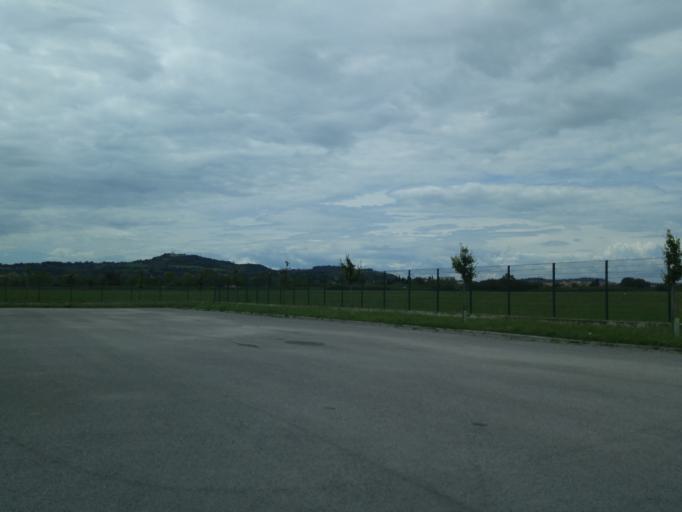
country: IT
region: The Marches
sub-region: Provincia di Pesaro e Urbino
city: Fano
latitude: 43.8203
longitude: 13.0240
